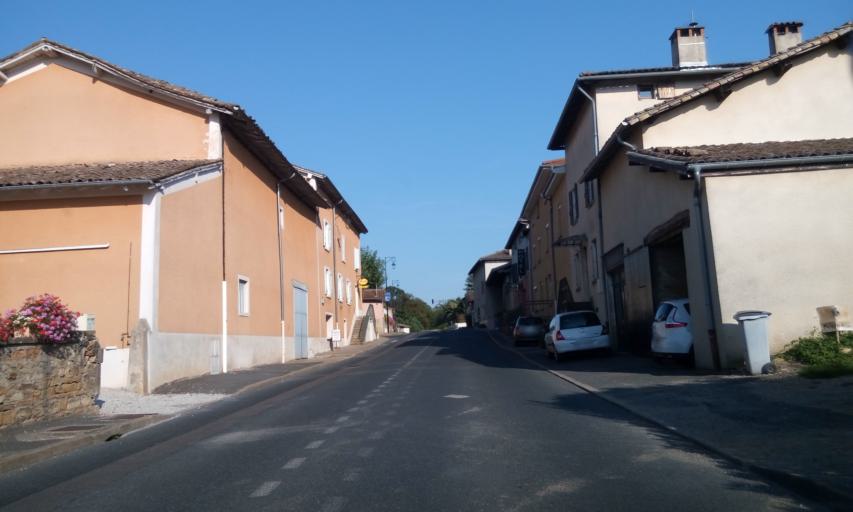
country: FR
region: Rhone-Alpes
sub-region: Departement de l'Ain
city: Villeneuve
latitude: 46.0008
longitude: 4.8478
